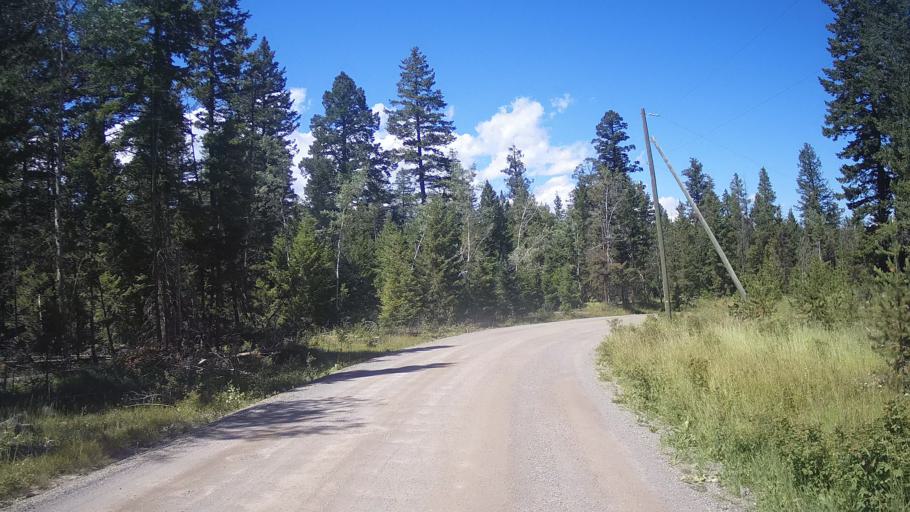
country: CA
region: British Columbia
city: Cache Creek
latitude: 51.1926
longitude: -121.5882
